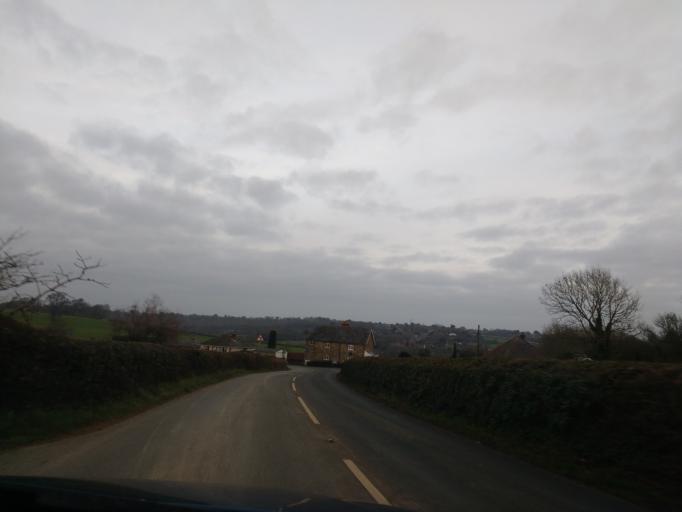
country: GB
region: England
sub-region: Isle of Wight
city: Northwood
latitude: 50.7369
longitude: -1.3358
